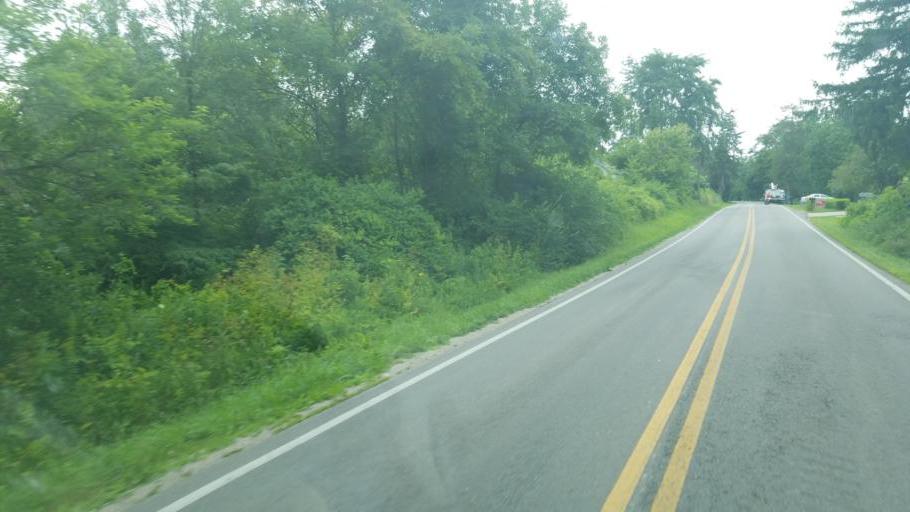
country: US
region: Ohio
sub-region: Delaware County
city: Ashley
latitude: 40.3979
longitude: -82.9473
